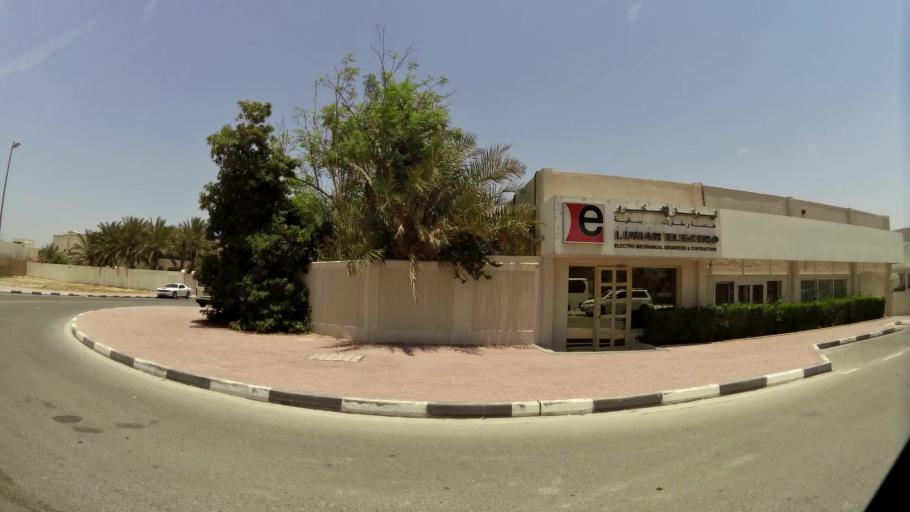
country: AE
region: Ash Shariqah
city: Sharjah
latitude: 25.2329
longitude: 55.2839
